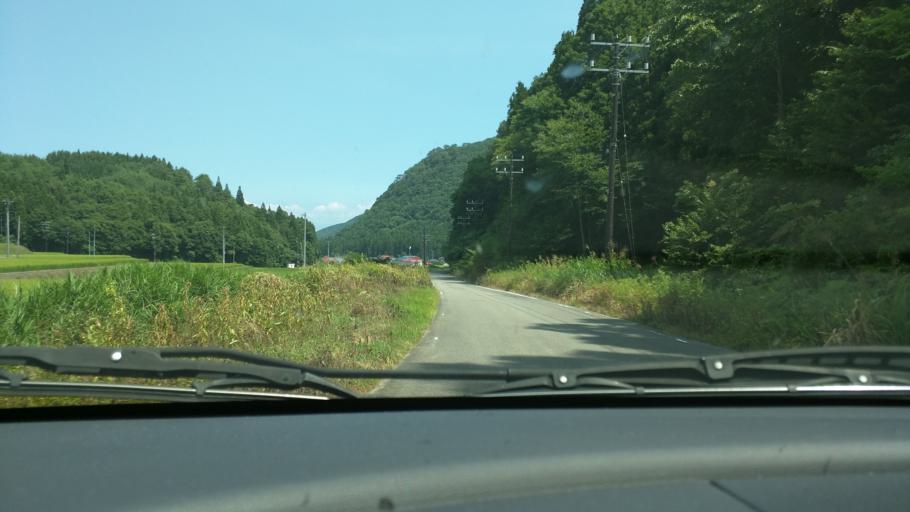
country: JP
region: Fukushima
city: Inawashiro
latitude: 37.3762
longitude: 140.0629
